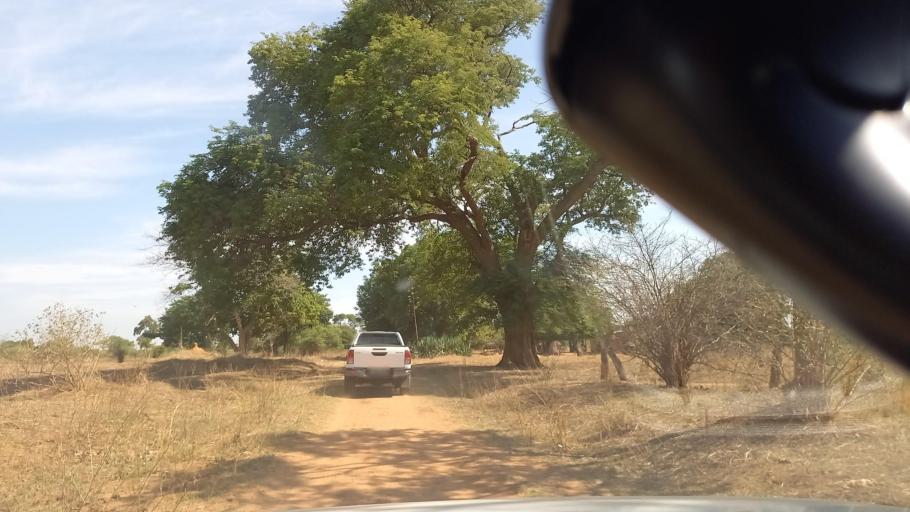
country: ZM
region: Southern
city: Mazabuka
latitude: -16.0360
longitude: 27.6229
